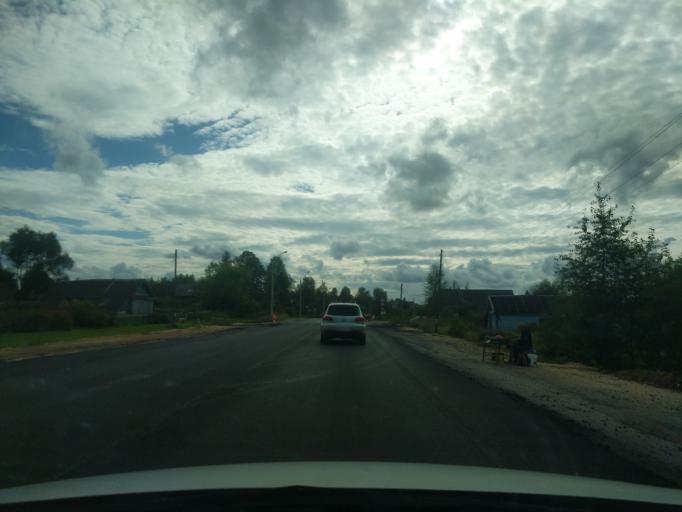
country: RU
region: Jaroslavl
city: Levashevo
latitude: 57.6568
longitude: 40.5641
